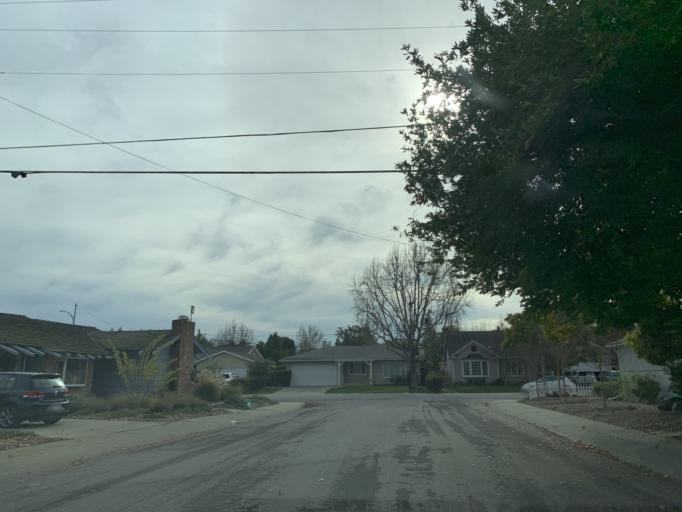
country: US
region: California
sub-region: Santa Clara County
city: Mountain View
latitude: 37.3873
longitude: -122.0942
